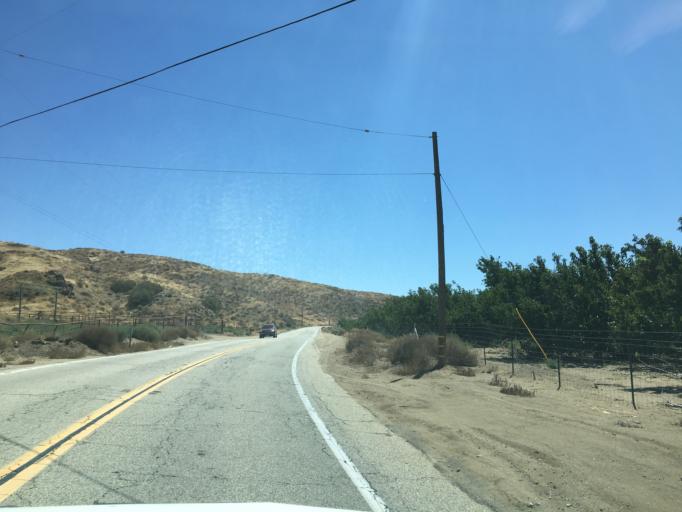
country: US
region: California
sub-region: Los Angeles County
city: Leona Valley
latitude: 34.6088
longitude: -118.2571
